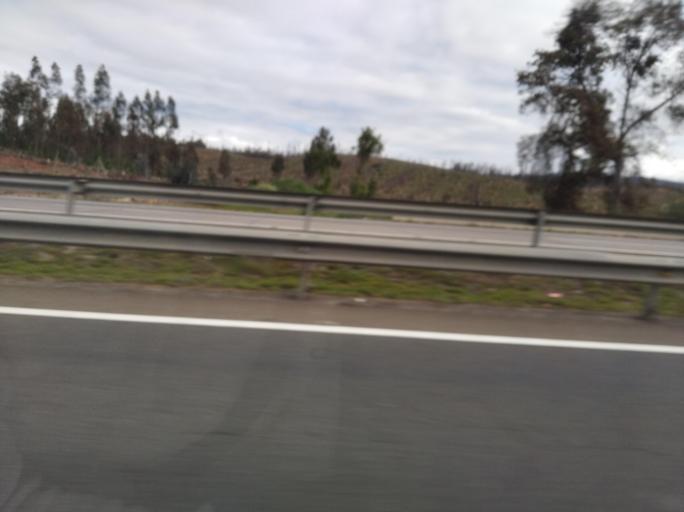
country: CL
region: Valparaiso
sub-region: Provincia de Valparaiso
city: Vina del Mar
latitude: -33.1680
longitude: -71.5284
